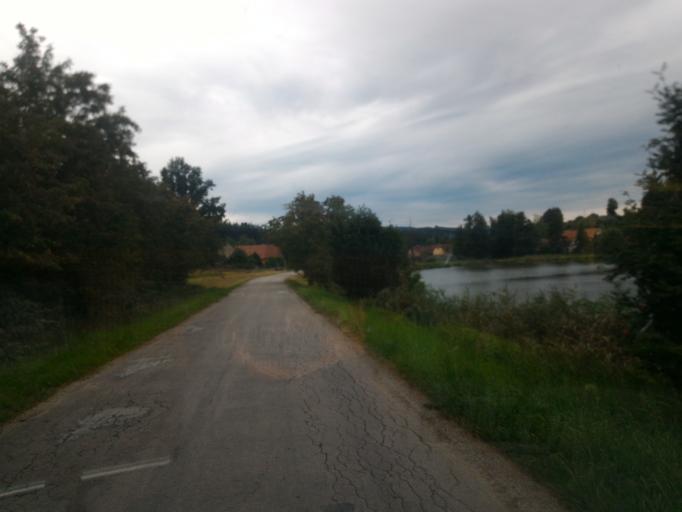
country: CZ
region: Vysocina
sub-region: Okres Jihlava
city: Telc
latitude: 49.1779
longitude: 15.3837
